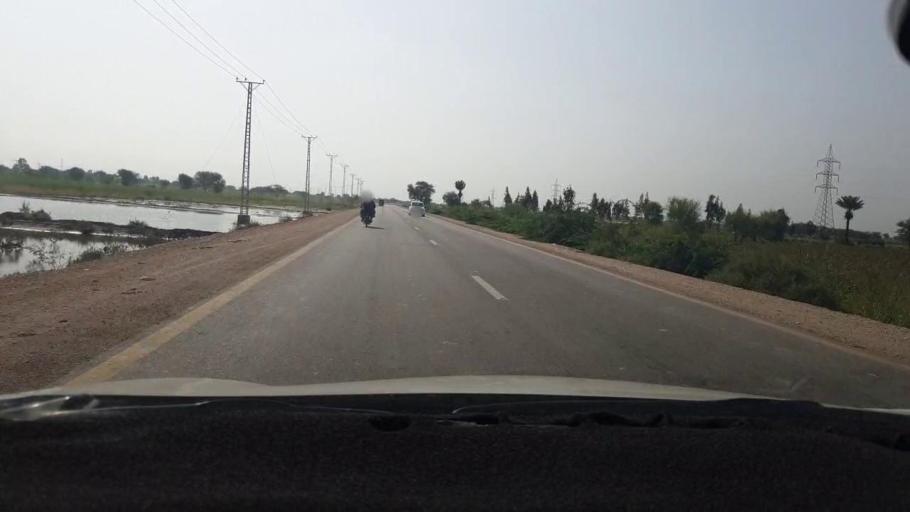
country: PK
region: Sindh
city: Jhol
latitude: 25.9362
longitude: 68.9907
